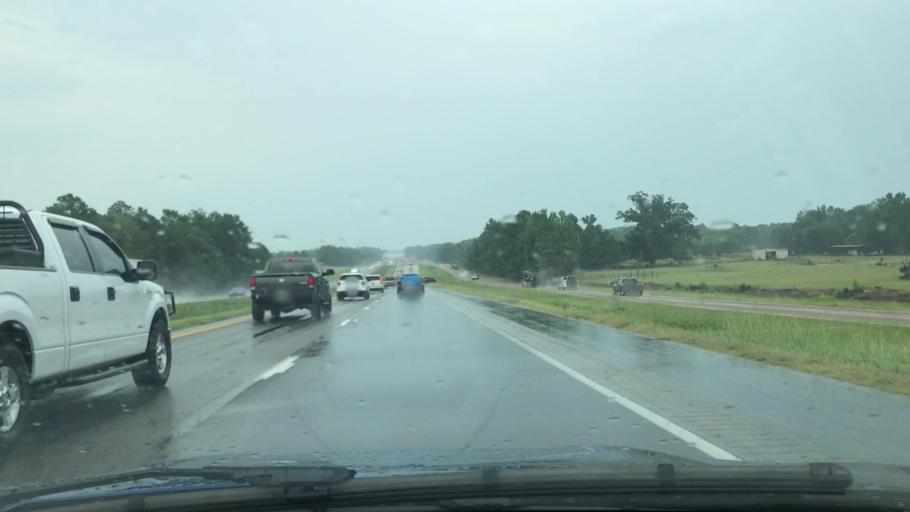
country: US
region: Texas
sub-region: Harrison County
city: Waskom
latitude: 32.4897
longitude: -94.1437
